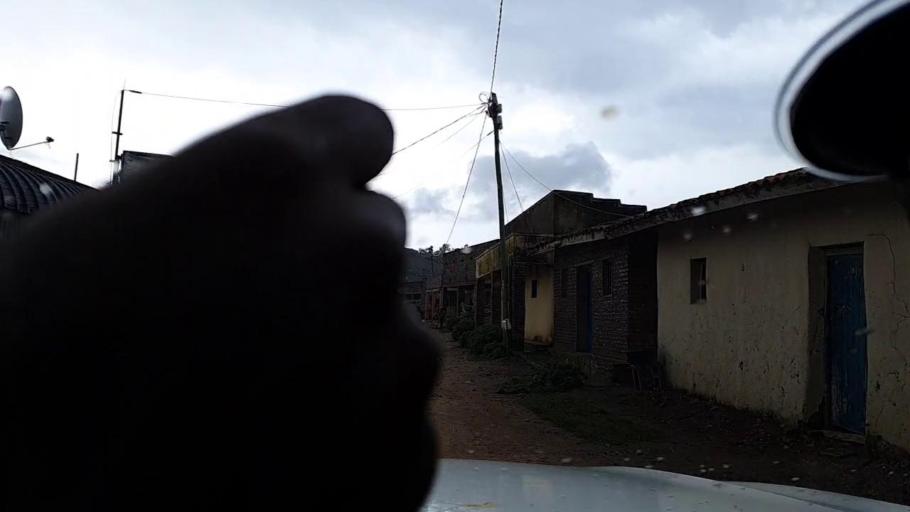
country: RW
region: Western Province
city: Kibuye
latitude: -2.0999
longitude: 29.4863
